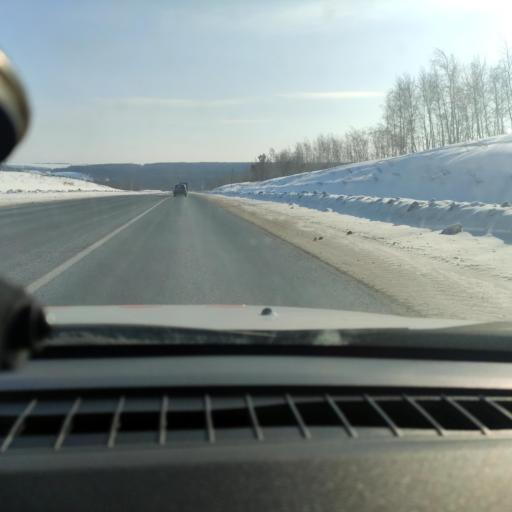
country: RU
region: Samara
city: Novosemeykino
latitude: 53.3669
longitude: 50.4360
